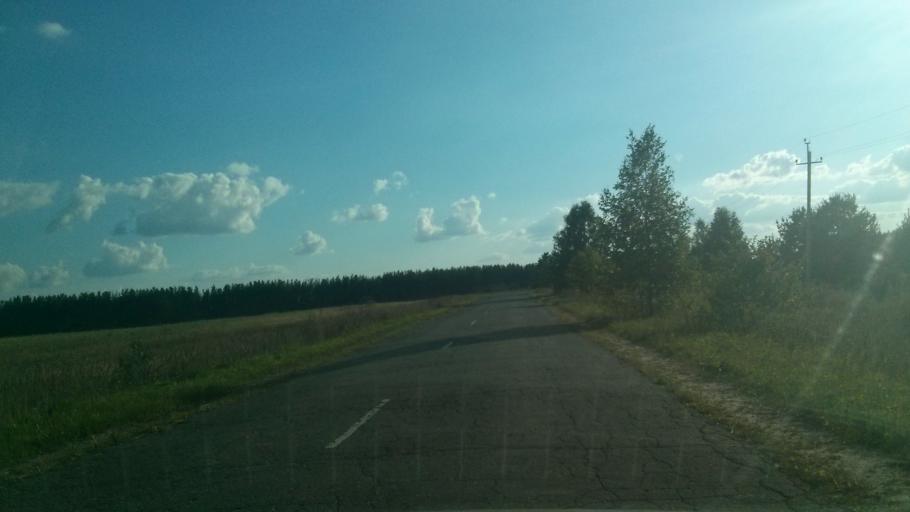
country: RU
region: Nizjnij Novgorod
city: Shimorskoye
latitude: 55.3004
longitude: 41.8305
